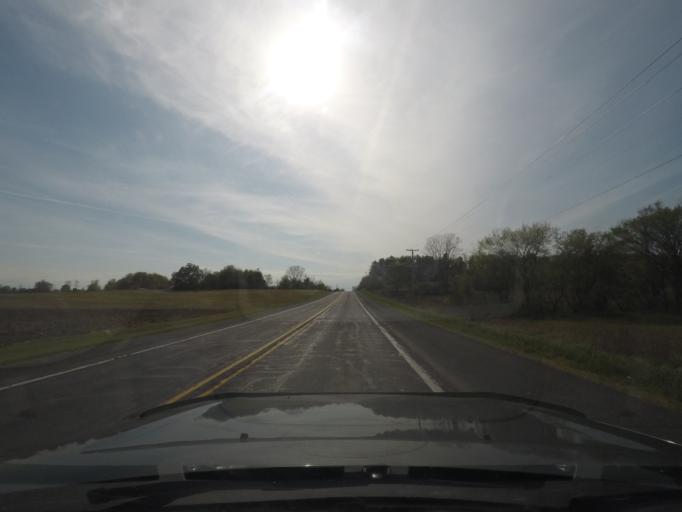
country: US
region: Indiana
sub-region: LaPorte County
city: Hudson Lake
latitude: 41.7981
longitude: -86.5080
